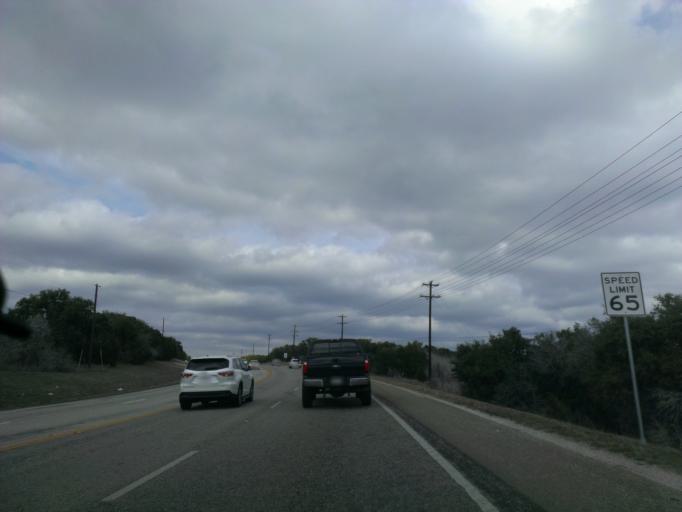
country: US
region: Texas
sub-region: Travis County
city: Briarcliff
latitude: 30.3934
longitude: -98.0864
